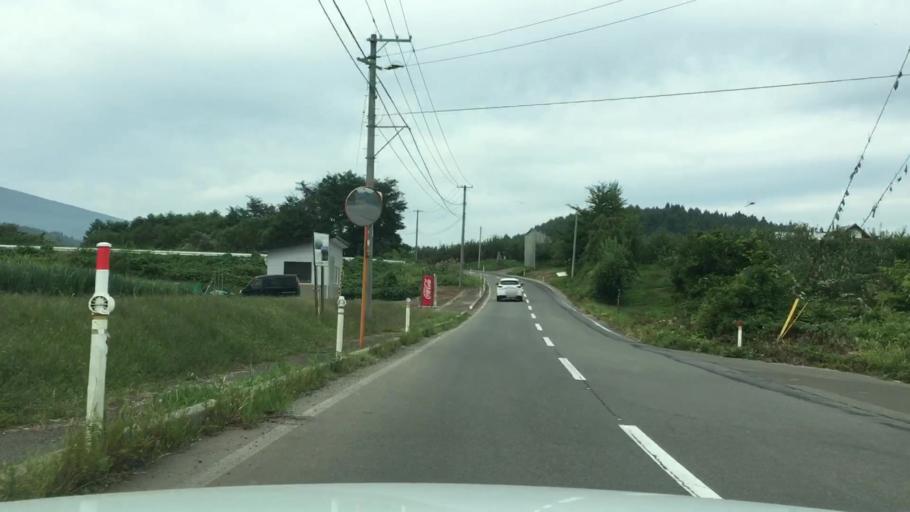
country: JP
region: Aomori
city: Hirosaki
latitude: 40.6673
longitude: 140.3954
